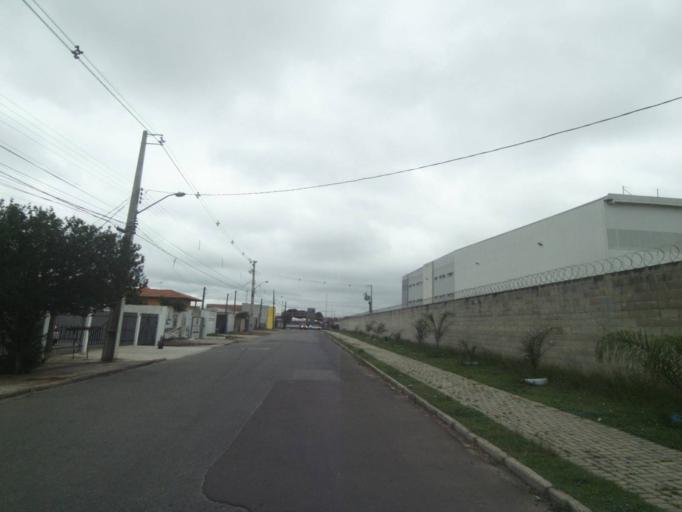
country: BR
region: Parana
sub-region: Sao Jose Dos Pinhais
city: Sao Jose dos Pinhais
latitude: -25.5462
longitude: -49.2877
